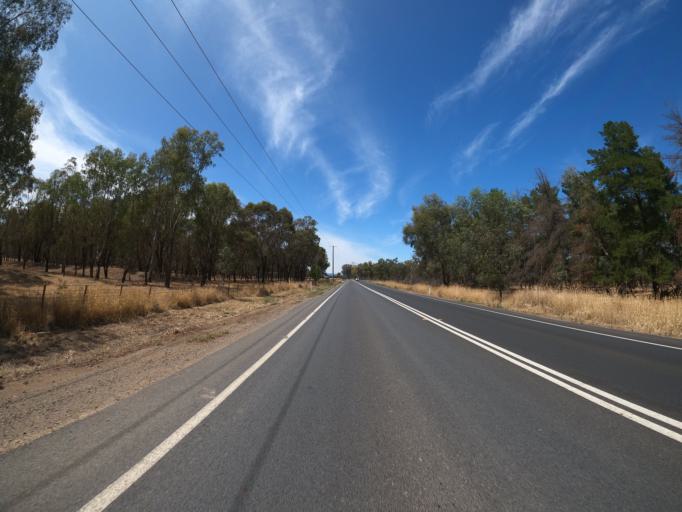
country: AU
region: Victoria
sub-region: Benalla
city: Benalla
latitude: -36.5278
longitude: 146.0396
